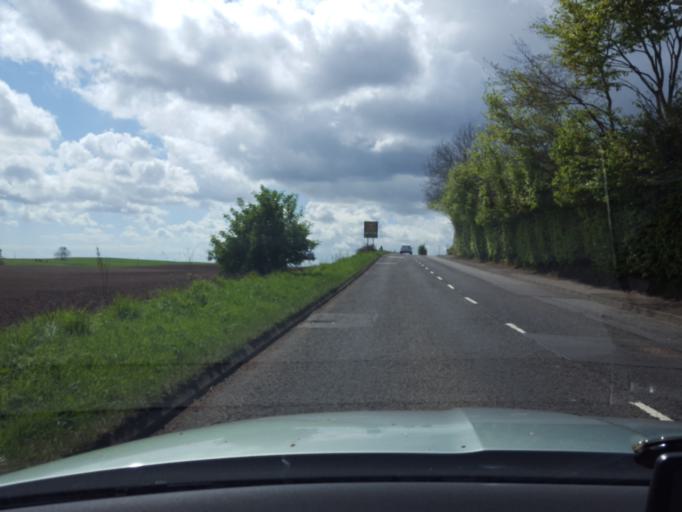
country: GB
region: Scotland
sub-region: Angus
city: Brechin
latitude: 56.7513
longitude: -2.6448
